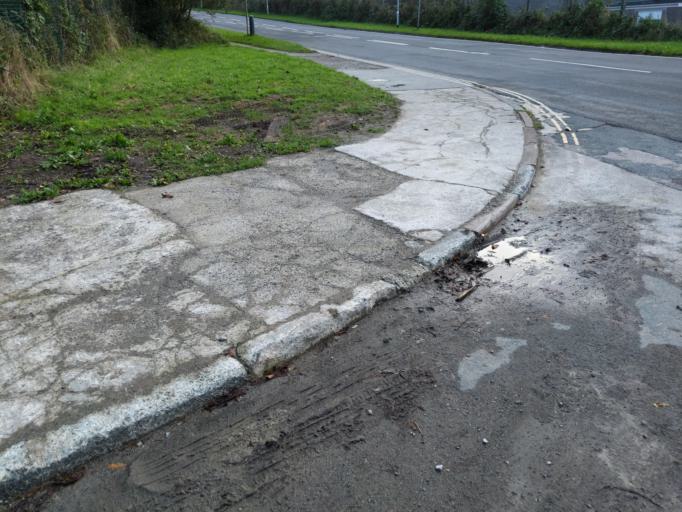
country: GB
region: England
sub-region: Cornwall
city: Saltash
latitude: 50.4188
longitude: -4.1876
